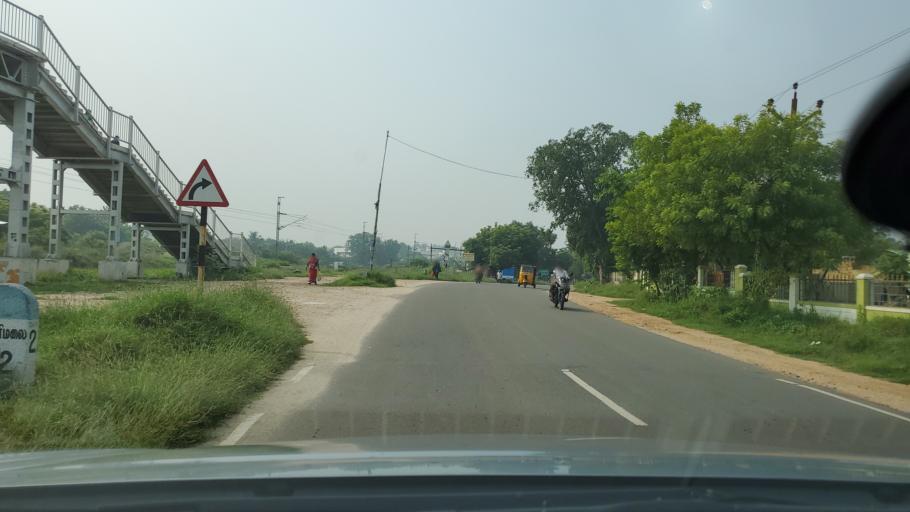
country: IN
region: Tamil Nadu
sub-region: Erode
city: Erode
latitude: 11.3163
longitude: 77.7124
